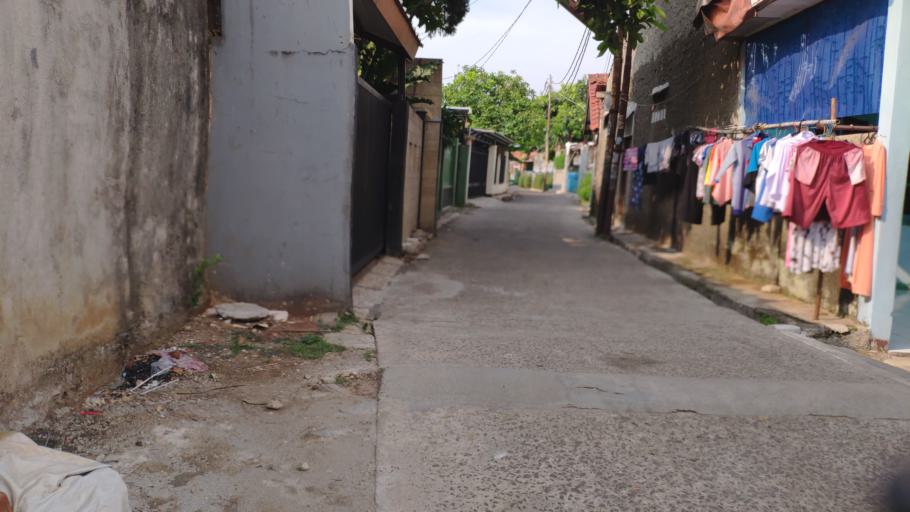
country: ID
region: West Java
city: Pamulang
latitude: -6.3309
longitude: 106.7952
